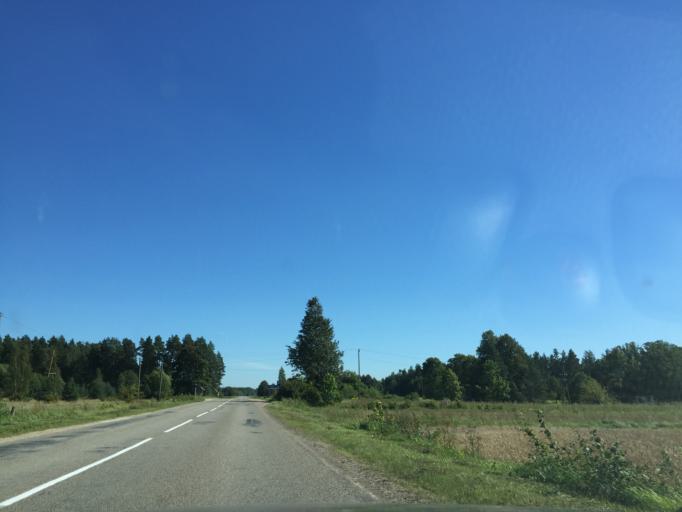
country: LV
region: Akniste
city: Akniste
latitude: 56.1471
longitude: 25.7901
